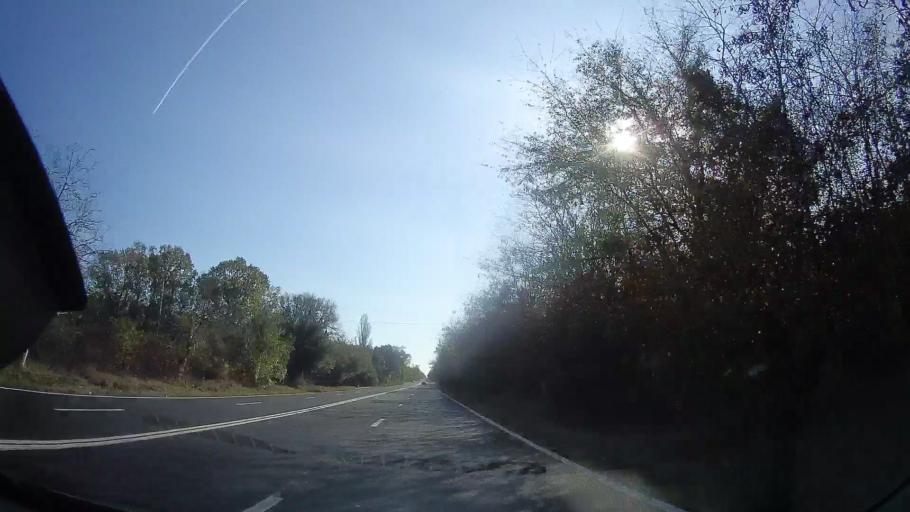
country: RO
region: Constanta
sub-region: Comuna Douazeci si Trei August
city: Dulcesti
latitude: 43.8782
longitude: 28.5737
